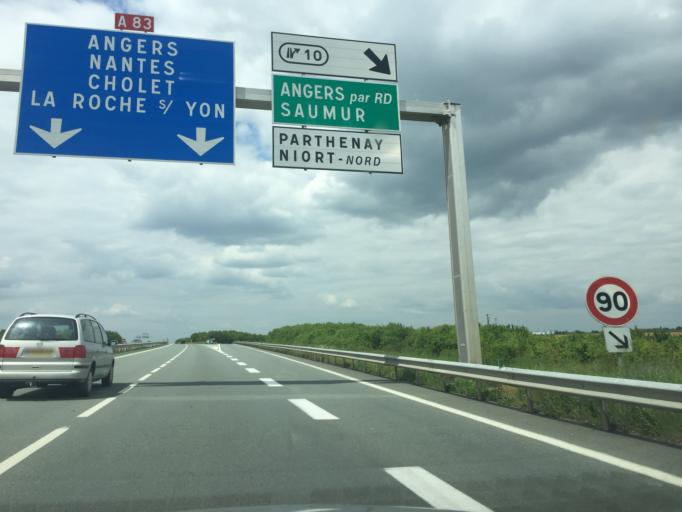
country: FR
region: Poitou-Charentes
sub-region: Departement des Deux-Sevres
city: Saint-Gelais
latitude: 46.4126
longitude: -0.3938
